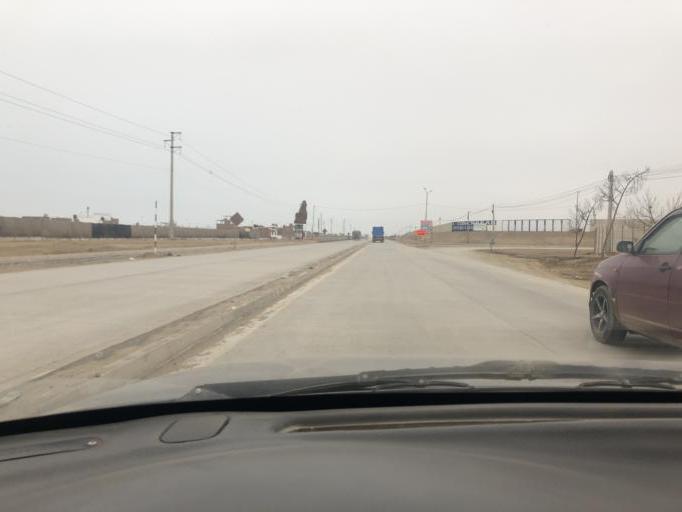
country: PE
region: Lima
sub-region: Lima
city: San Bartolo
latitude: -12.3768
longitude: -76.7824
